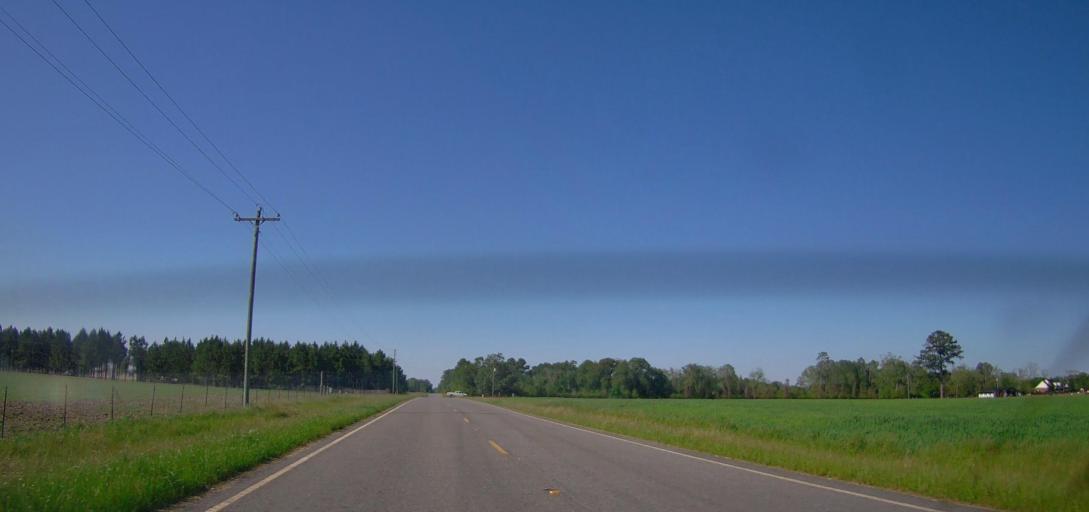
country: US
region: Georgia
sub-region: Wilcox County
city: Rochelle
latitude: 32.0755
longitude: -83.5035
